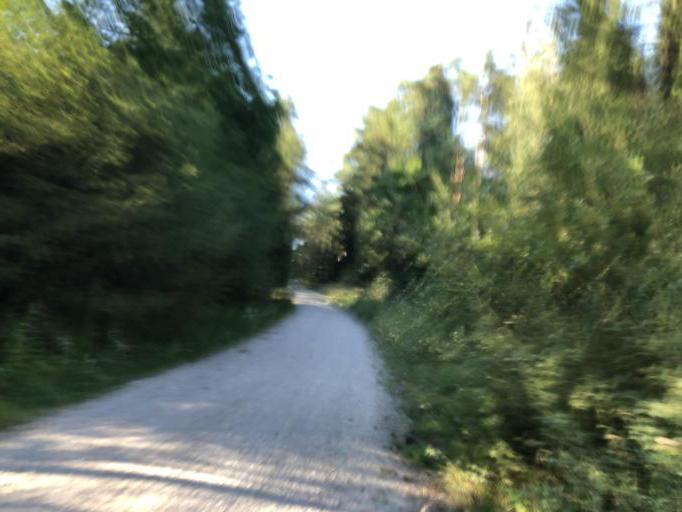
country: DE
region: Bavaria
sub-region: Regierungsbezirk Mittelfranken
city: Kalchreuth
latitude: 49.5527
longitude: 11.0995
